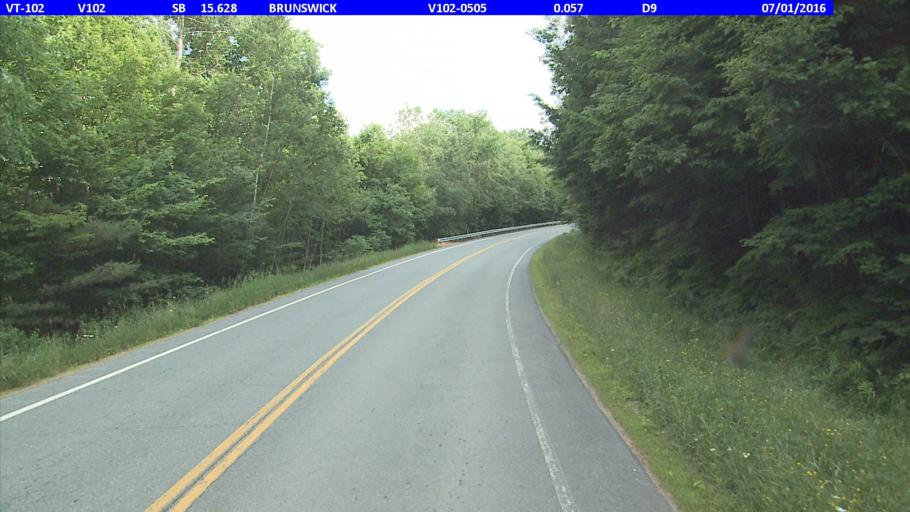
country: US
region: New Hampshire
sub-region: Coos County
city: Stratford
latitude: 44.6635
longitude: -71.5909
